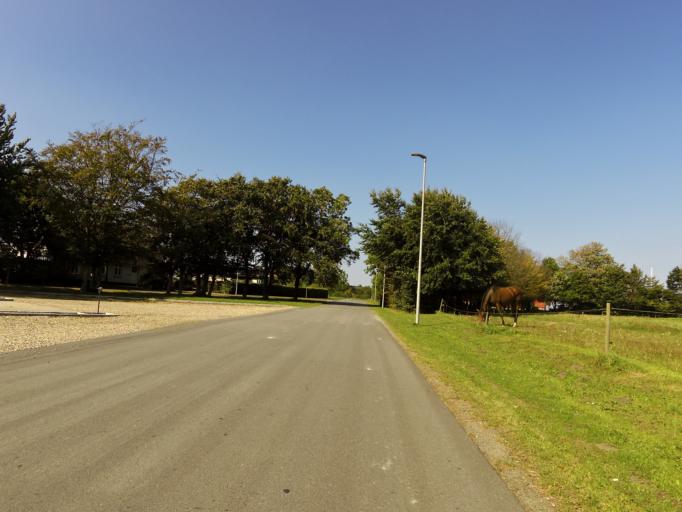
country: DK
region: South Denmark
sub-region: Vejen Kommune
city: Rodding
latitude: 55.3471
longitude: 9.1290
